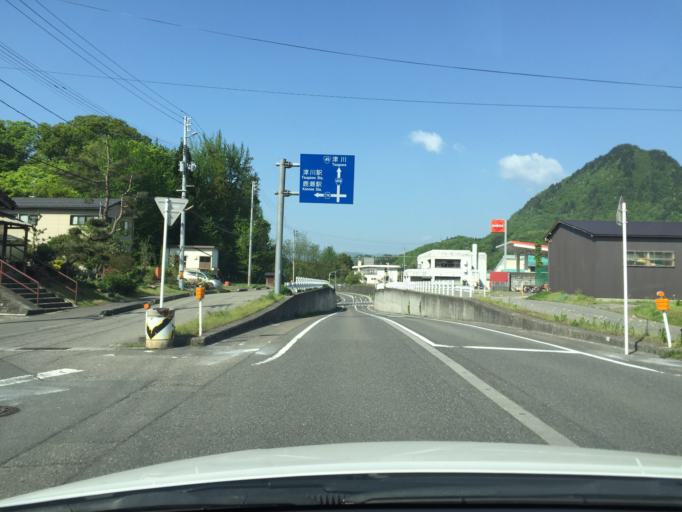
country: JP
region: Niigata
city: Shibata
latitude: 37.6981
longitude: 139.4857
